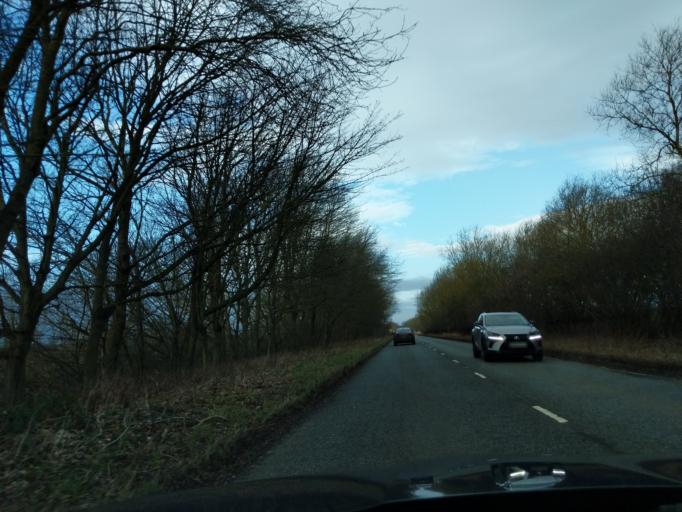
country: GB
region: England
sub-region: Northumberland
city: Darras Hall
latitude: 55.0732
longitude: -1.7953
